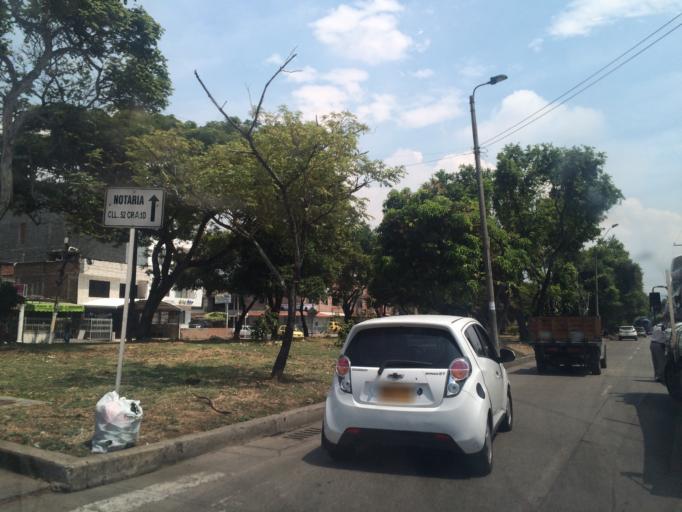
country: CO
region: Valle del Cauca
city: Cali
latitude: 3.4684
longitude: -76.5019
